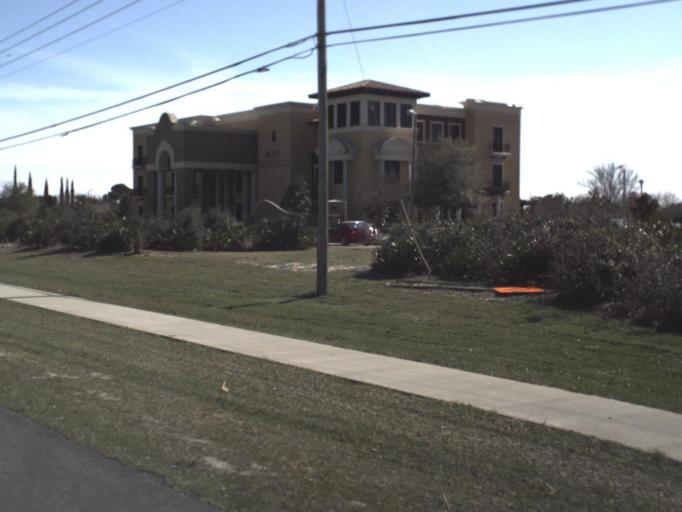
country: US
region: Florida
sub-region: Bay County
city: Panama City Beach
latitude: 30.2114
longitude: -85.8507
